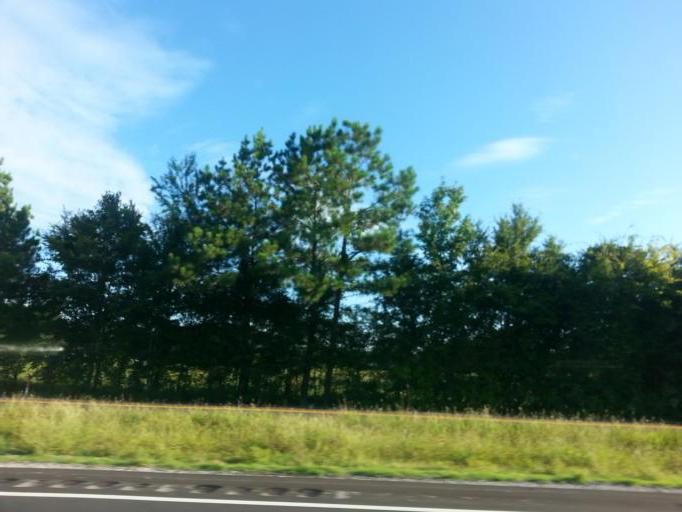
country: US
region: Alabama
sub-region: Lauderdale County
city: Killen
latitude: 34.8595
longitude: -87.4985
